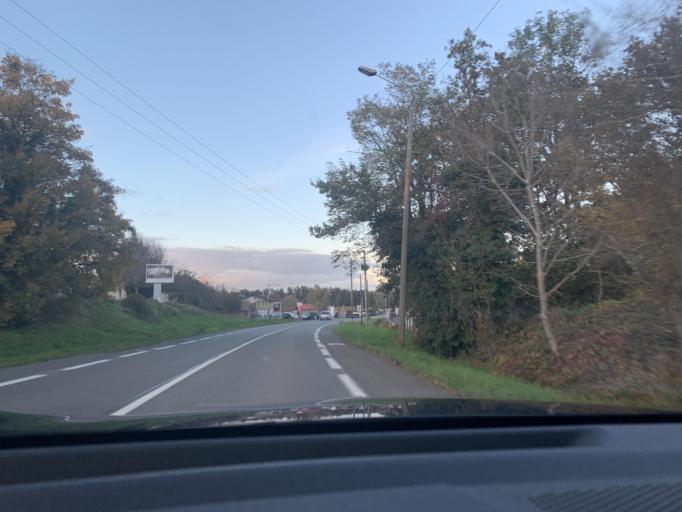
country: FR
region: Rhone-Alpes
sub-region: Departement du Rhone
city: Liergues
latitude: 45.9627
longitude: 4.6682
